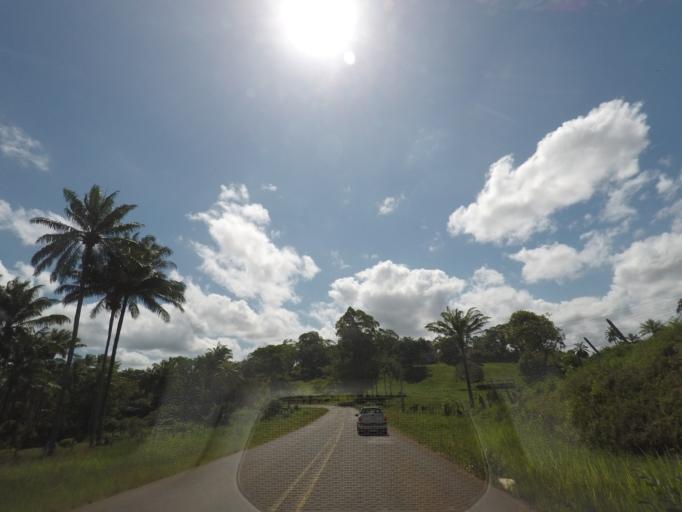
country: BR
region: Bahia
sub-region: Taperoa
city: Taperoa
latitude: -13.5540
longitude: -39.1030
